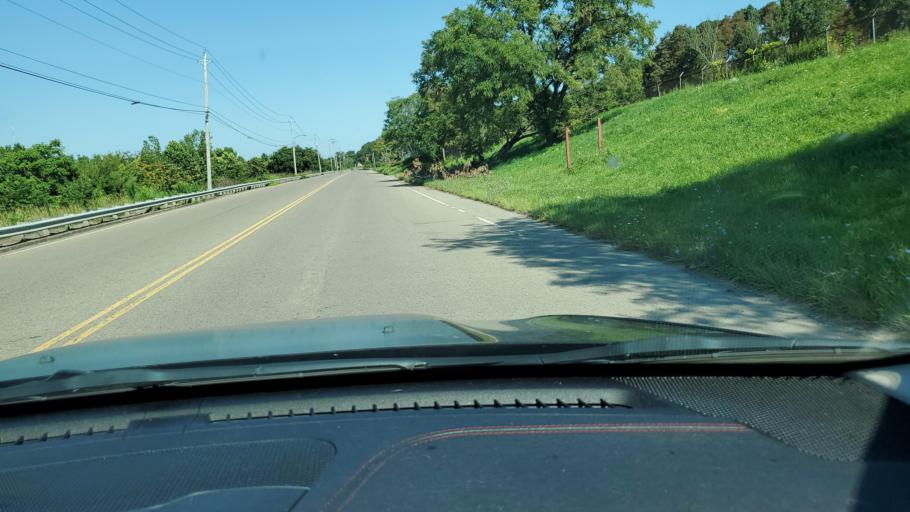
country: US
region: Ohio
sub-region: Mahoning County
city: Campbell
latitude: 41.0668
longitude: -80.5927
